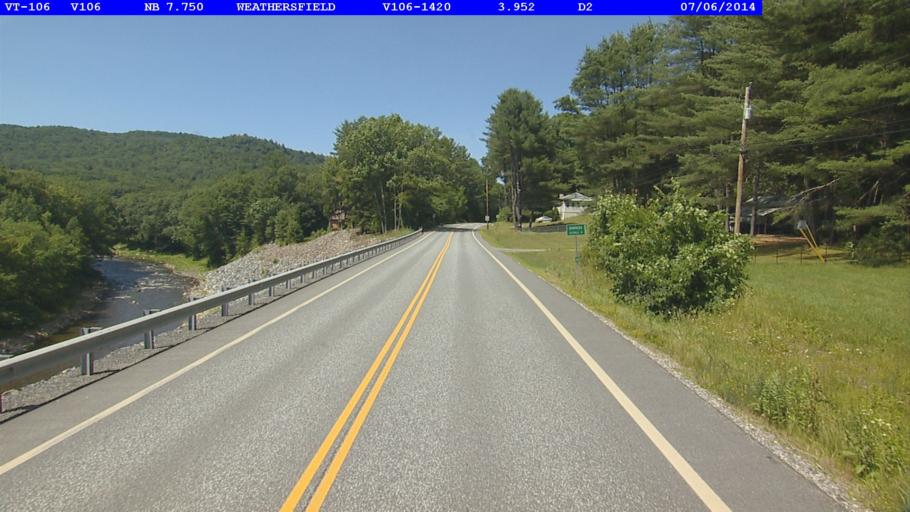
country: US
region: Vermont
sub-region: Windsor County
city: Springfield
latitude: 43.3954
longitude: -72.5141
